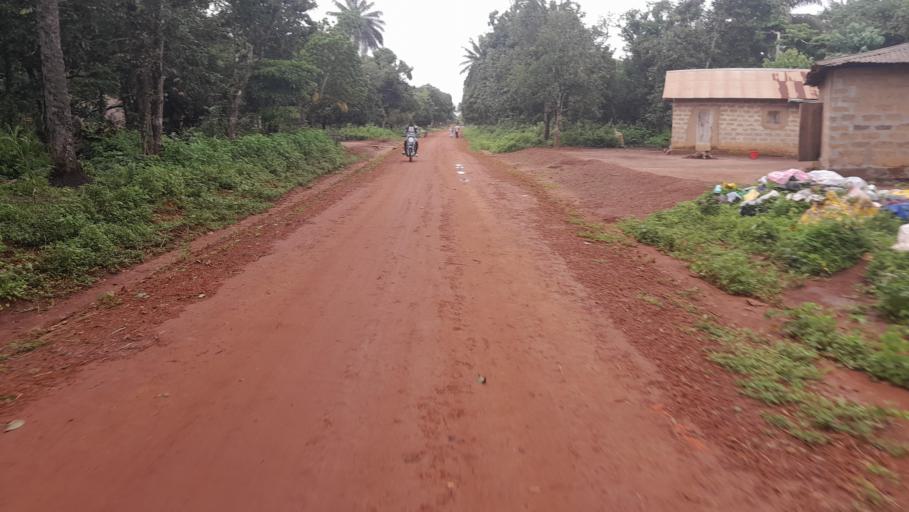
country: GN
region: Boke
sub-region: Boffa
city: Boffa
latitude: 10.0119
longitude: -13.8874
